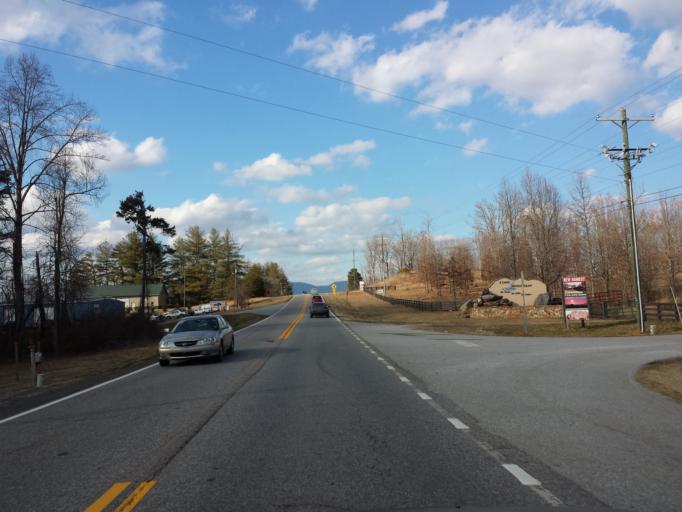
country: US
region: Georgia
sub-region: White County
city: Cleveland
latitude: 34.5715
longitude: -83.7888
